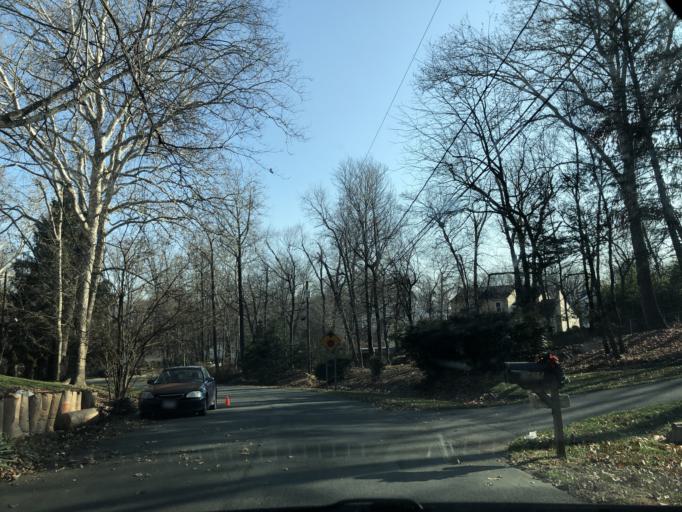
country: US
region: Maryland
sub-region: Montgomery County
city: Burtonsville
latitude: 39.0993
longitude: -76.9386
